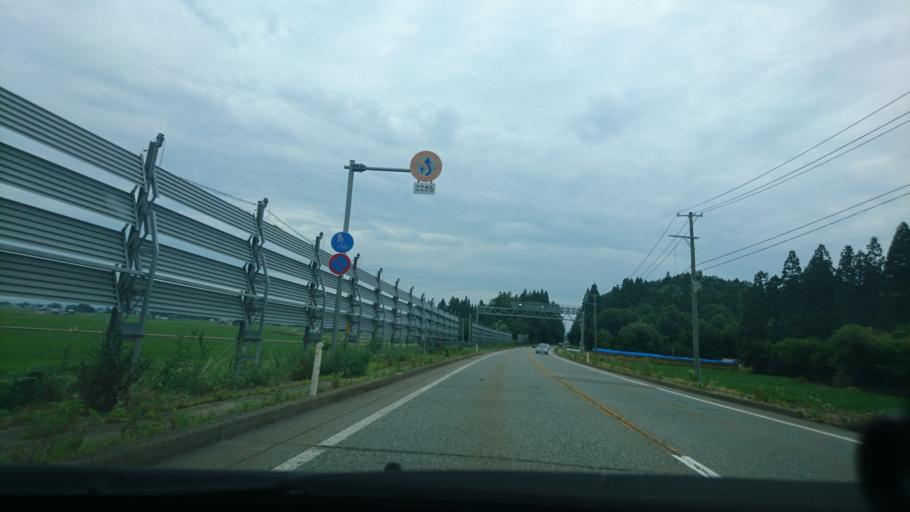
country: JP
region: Akita
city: Yokotemachi
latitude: 39.3857
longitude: 140.5674
